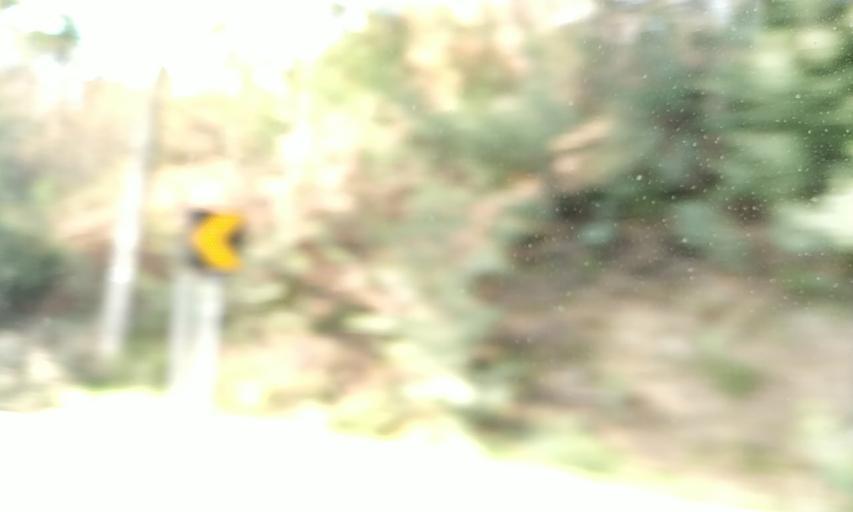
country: PT
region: Vila Real
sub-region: Mondim de Basto
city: Mondim de Basto
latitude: 41.4136
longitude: -7.9682
